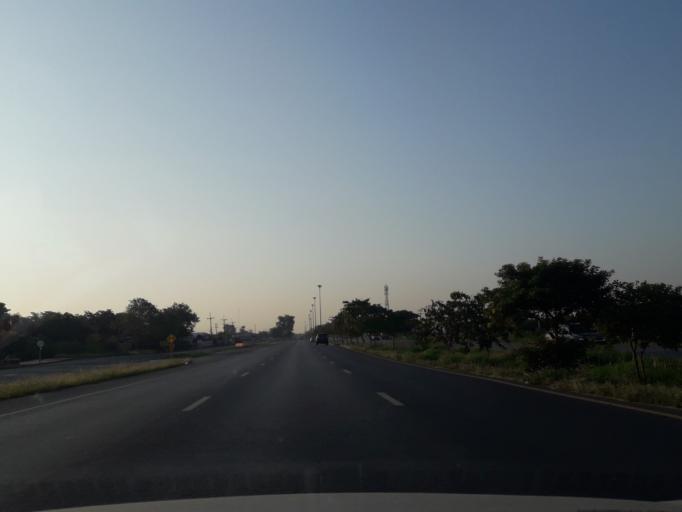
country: TH
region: Phra Nakhon Si Ayutthaya
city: Bang Pa-in
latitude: 14.2032
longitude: 100.5489
